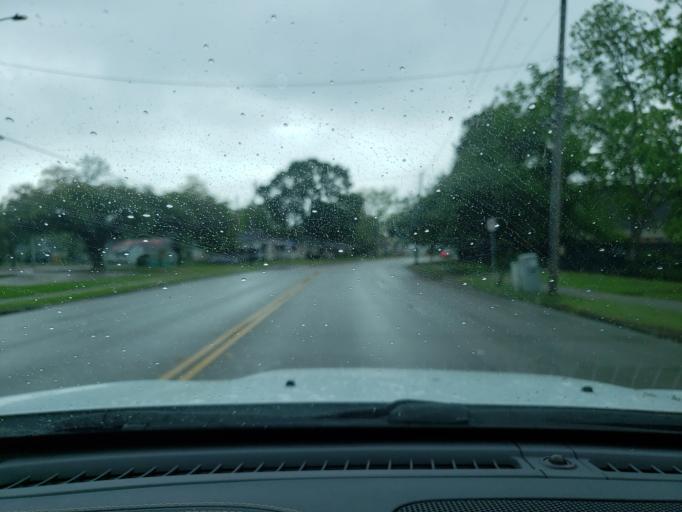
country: US
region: Texas
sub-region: Harris County
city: Baytown
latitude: 29.7395
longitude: -94.9708
